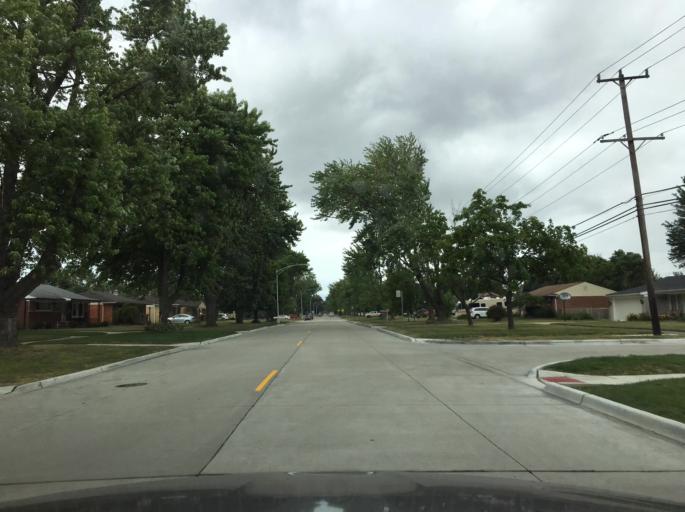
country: US
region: Michigan
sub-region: Macomb County
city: Clinton
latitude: 42.5609
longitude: -82.9106
